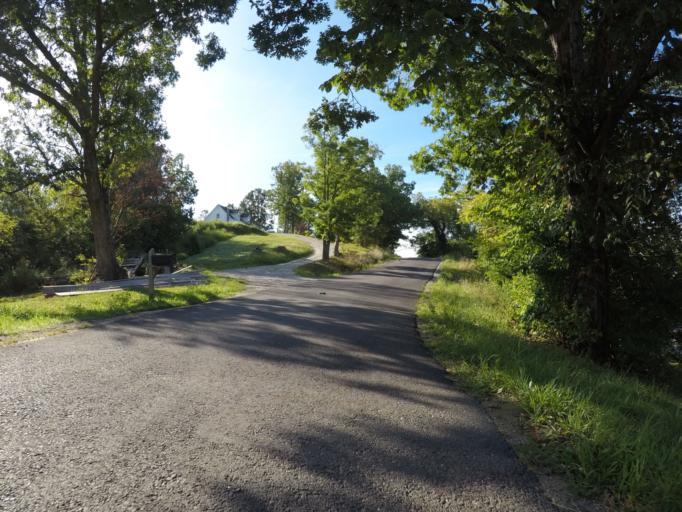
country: US
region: Ohio
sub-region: Lawrence County
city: Burlington
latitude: 38.5246
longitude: -82.5246
